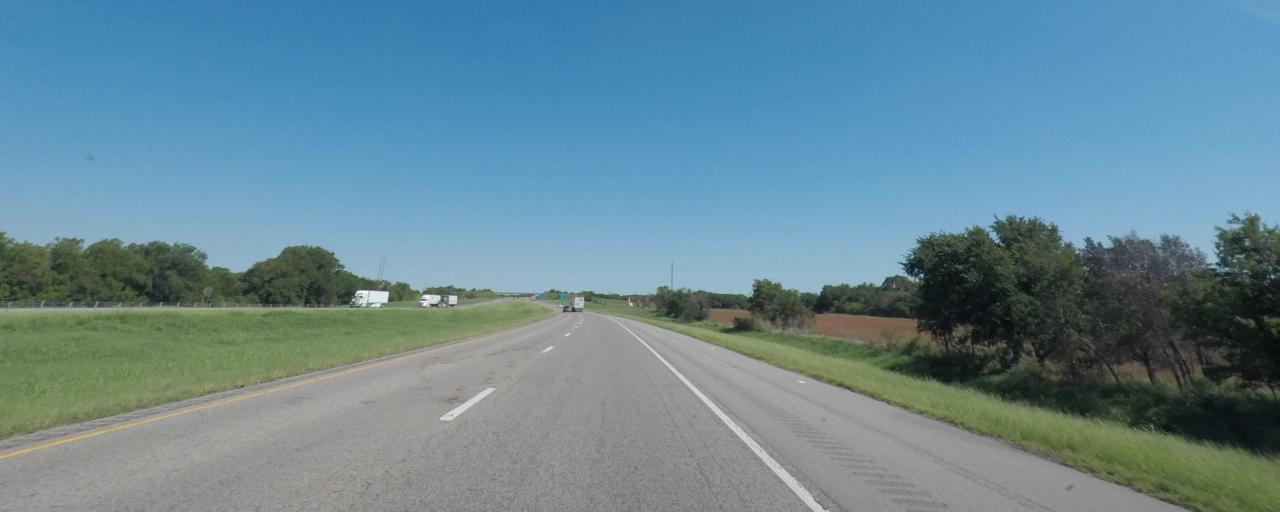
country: US
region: Oklahoma
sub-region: Noble County
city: Perry
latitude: 36.2537
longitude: -97.3252
